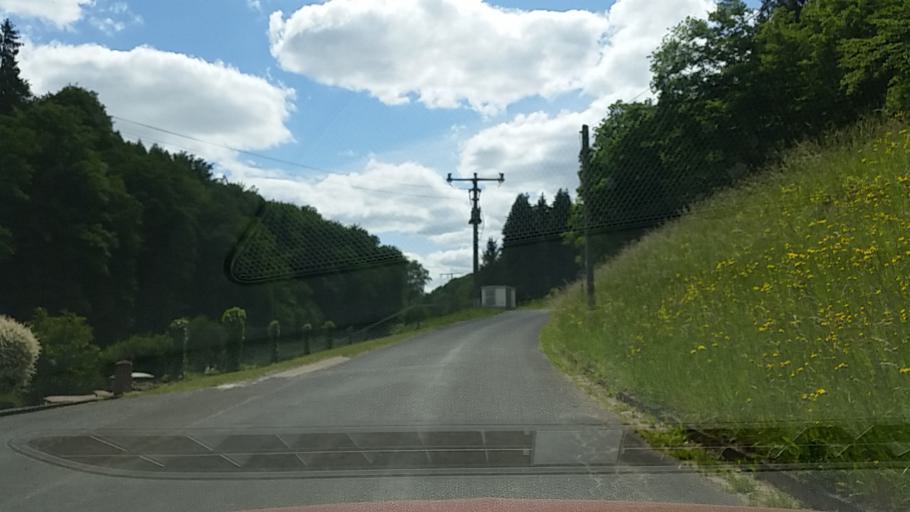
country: DE
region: Bavaria
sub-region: Regierungsbezirk Unterfranken
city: Neuendorf
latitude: 50.0172
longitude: 9.6613
